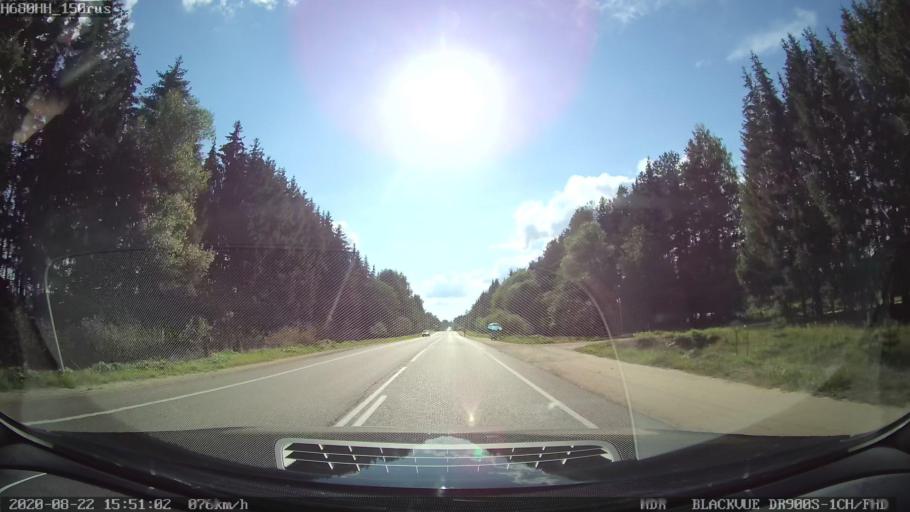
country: RU
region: Tverskaya
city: Bezhetsk
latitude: 57.6674
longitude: 36.4340
